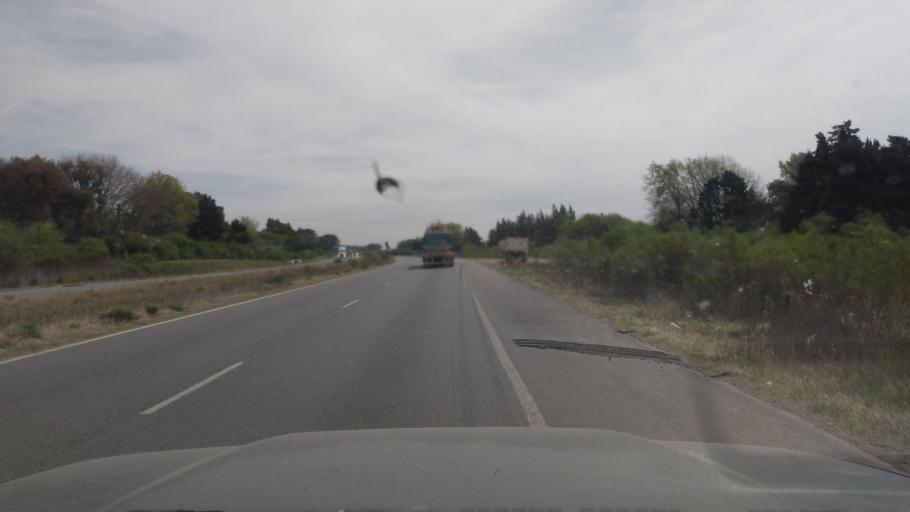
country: AR
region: Buenos Aires
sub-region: Partido de Lujan
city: Lujan
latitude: -34.5049
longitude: -59.0441
